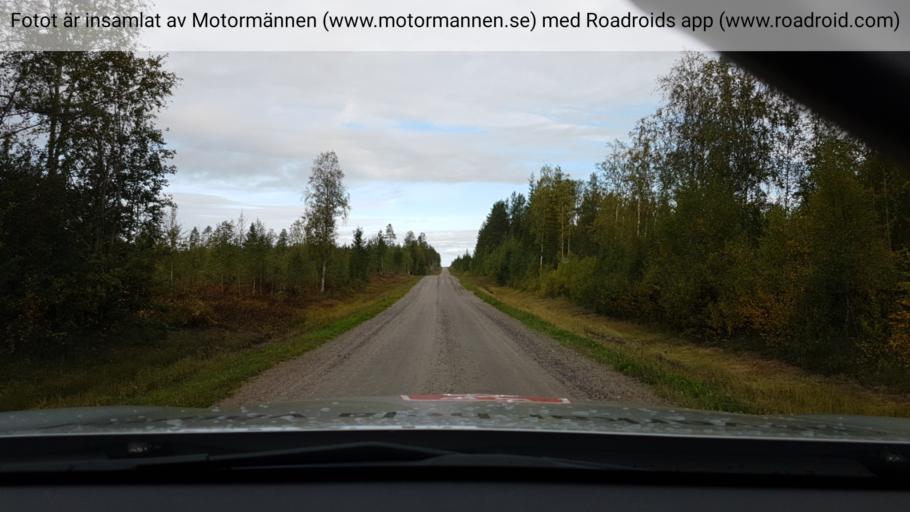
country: SE
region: Vaesterbotten
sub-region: Skelleftea Kommun
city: Byske
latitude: 65.1280
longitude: 21.2030
